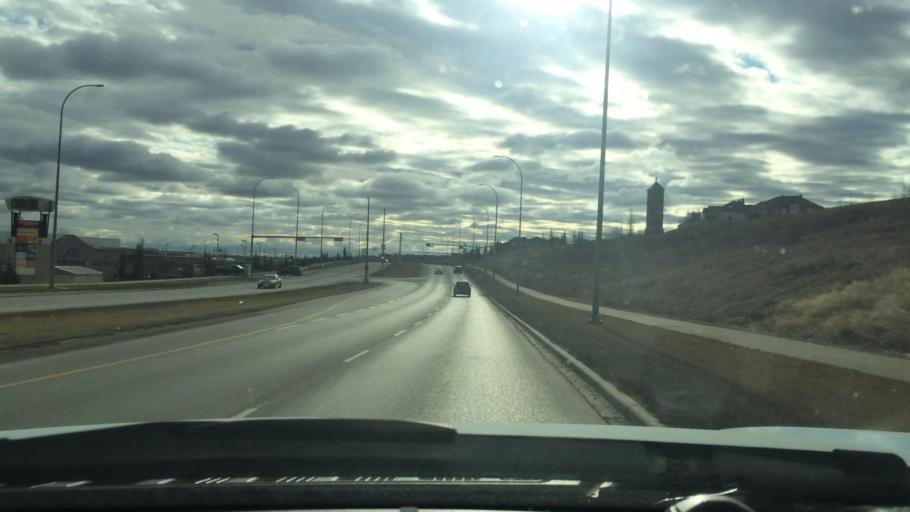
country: CA
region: Alberta
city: Calgary
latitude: 51.1641
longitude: -114.1290
